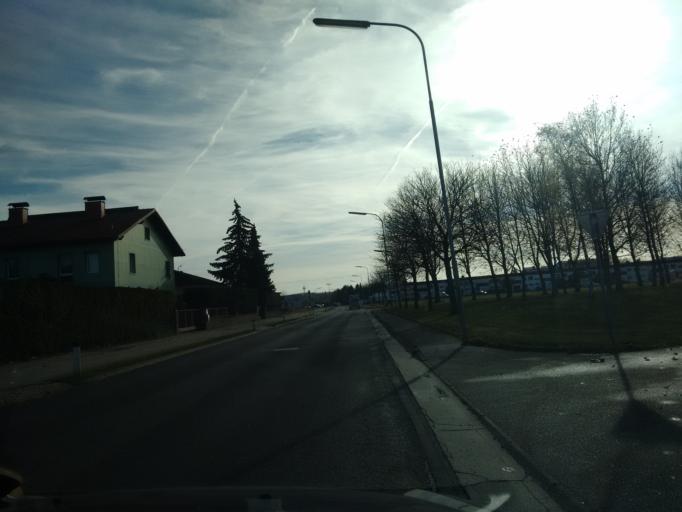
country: AT
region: Upper Austria
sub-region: Politischer Bezirk Linz-Land
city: Traun
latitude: 48.2355
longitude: 14.2557
